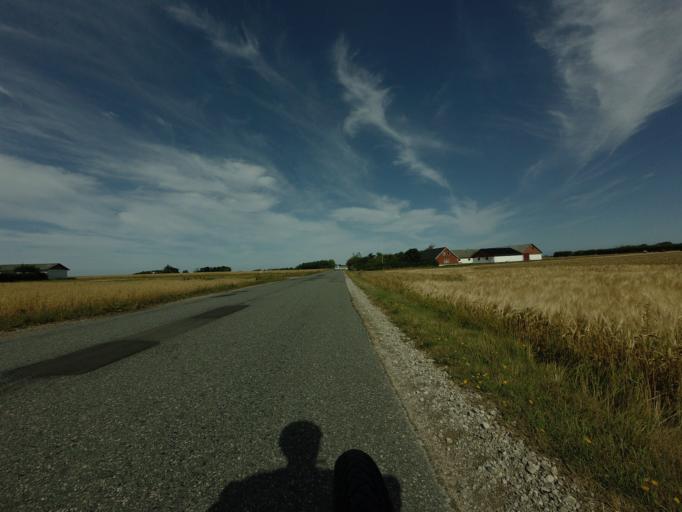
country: DK
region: North Denmark
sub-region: Hjorring Kommune
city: Vra
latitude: 57.4155
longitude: 9.8672
